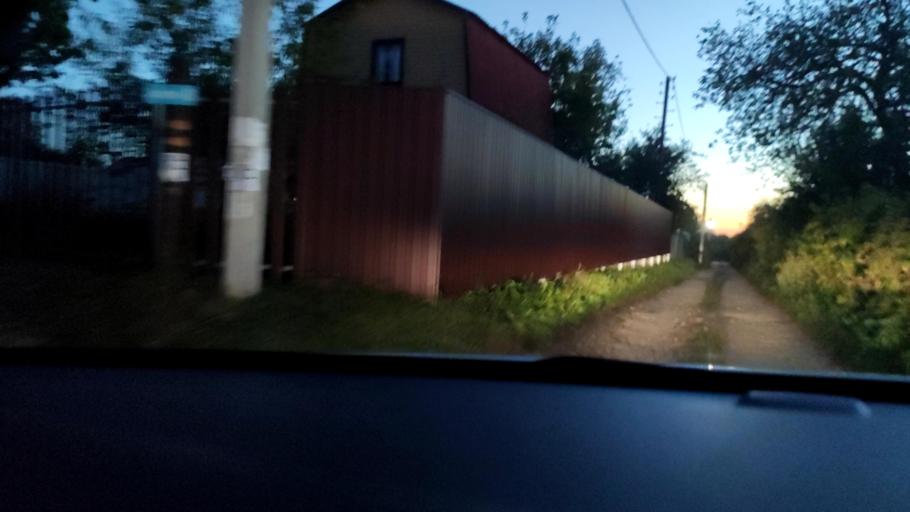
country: RU
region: Tatarstan
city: Vysokaya Gora
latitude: 55.8365
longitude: 49.2291
